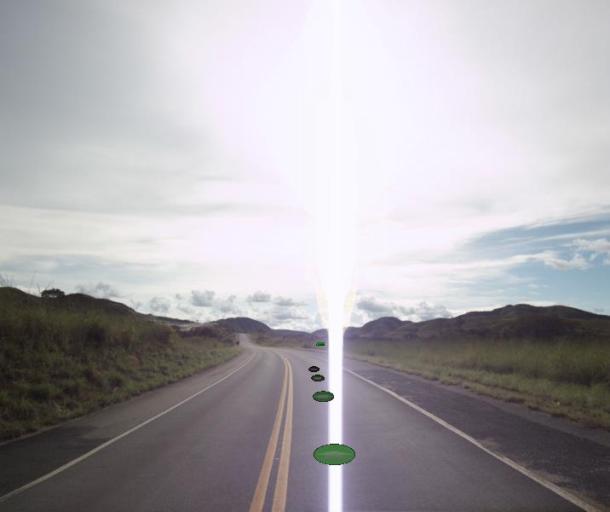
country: BR
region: Goias
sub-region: Barro Alto
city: Barro Alto
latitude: -15.1220
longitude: -48.7136
